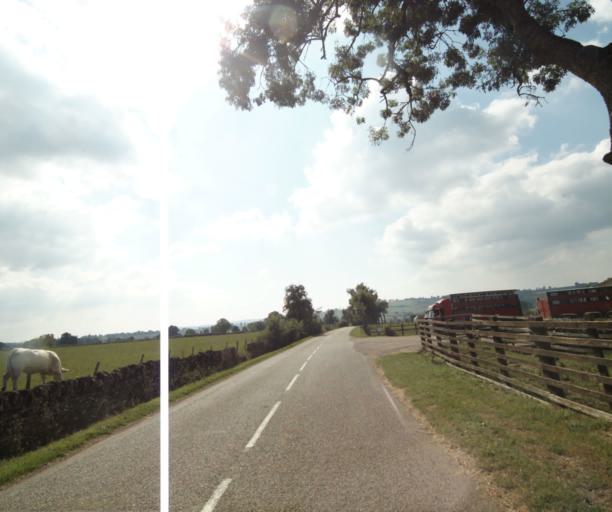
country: FR
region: Bourgogne
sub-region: Departement de Saone-et-Loire
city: Charolles
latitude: 46.3743
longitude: 4.2477
